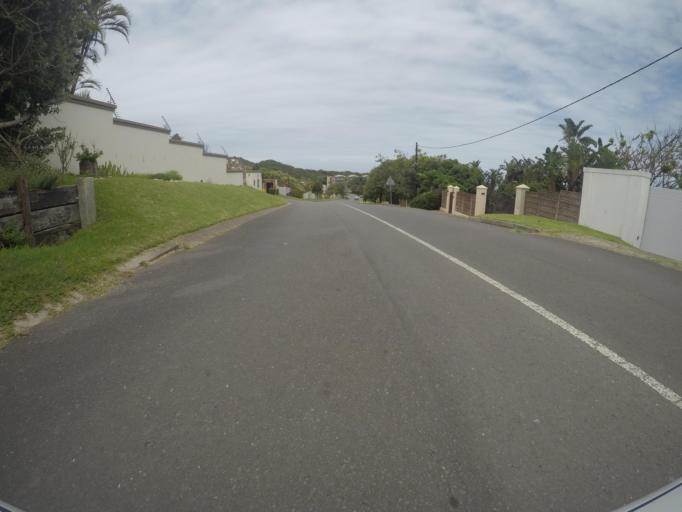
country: ZA
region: Eastern Cape
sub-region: Buffalo City Metropolitan Municipality
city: East London
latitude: -32.9812
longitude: 27.9501
